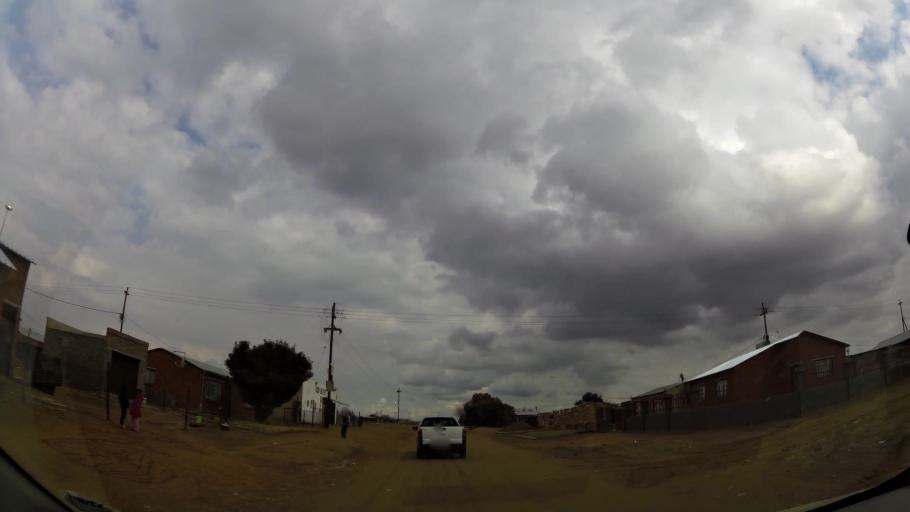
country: ZA
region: Orange Free State
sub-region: Fezile Dabi District Municipality
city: Sasolburg
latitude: -26.8670
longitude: 27.8710
